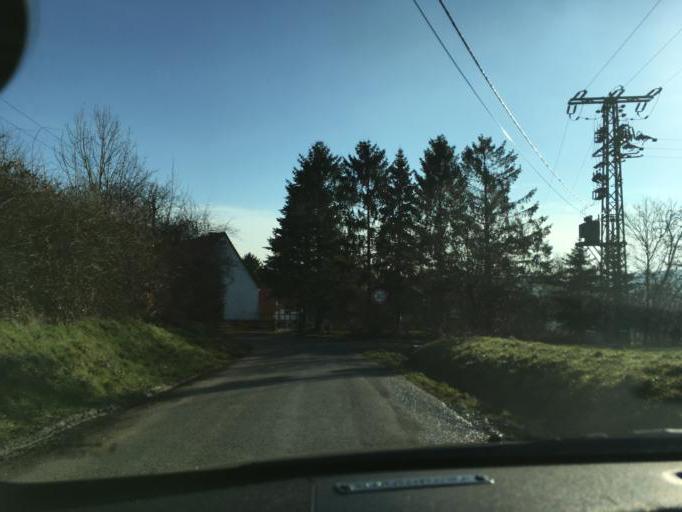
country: DE
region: North Rhine-Westphalia
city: Iserlohn
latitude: 51.4163
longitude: 7.6456
